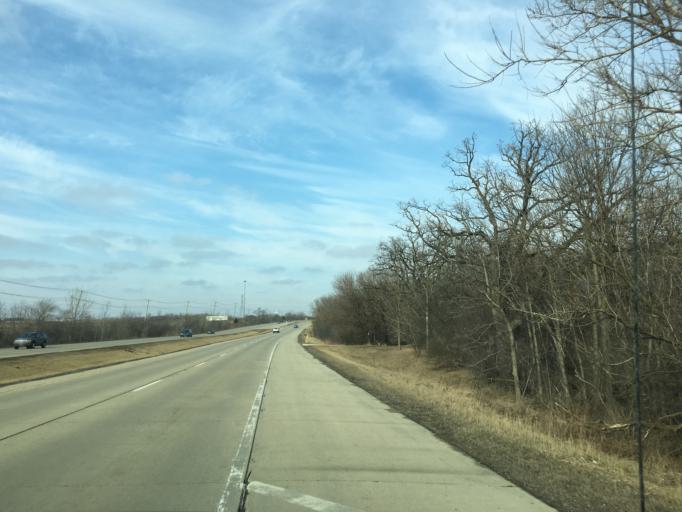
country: US
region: Illinois
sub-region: Kane County
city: East Dundee
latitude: 42.0819
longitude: -88.2272
